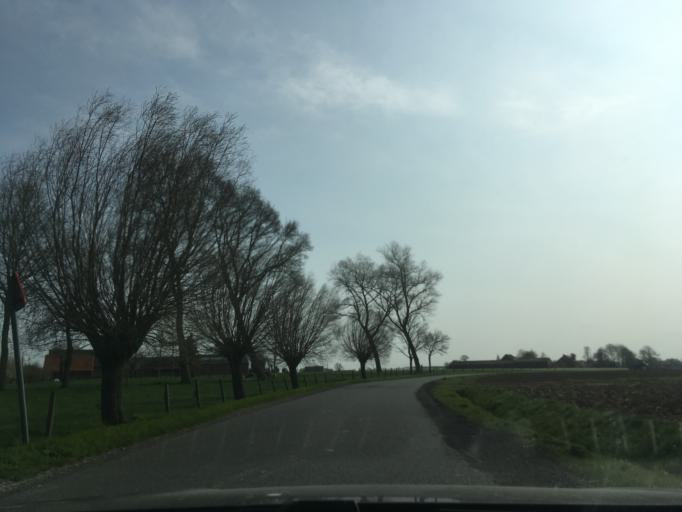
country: BE
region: Flanders
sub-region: Provincie West-Vlaanderen
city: Lichtervelde
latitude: 51.0147
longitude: 3.1834
